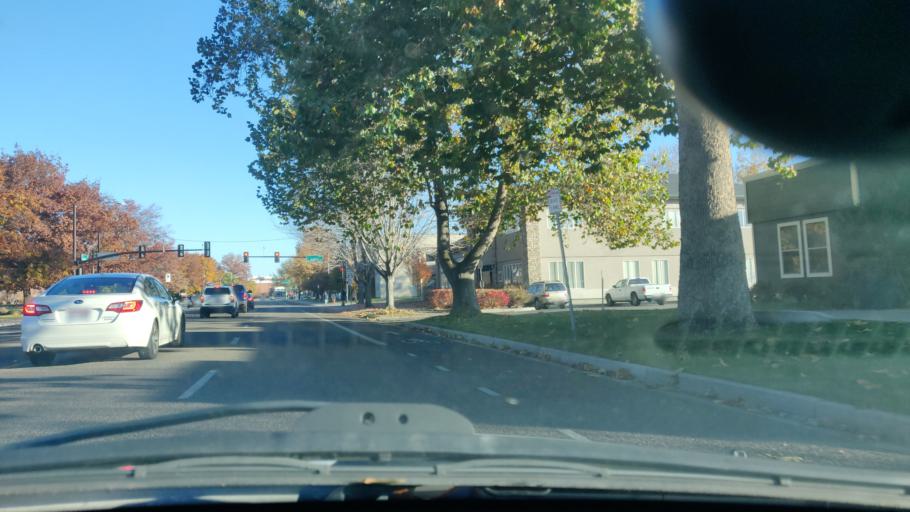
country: US
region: Idaho
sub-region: Ada County
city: Boise
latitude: 43.6037
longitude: -116.2070
